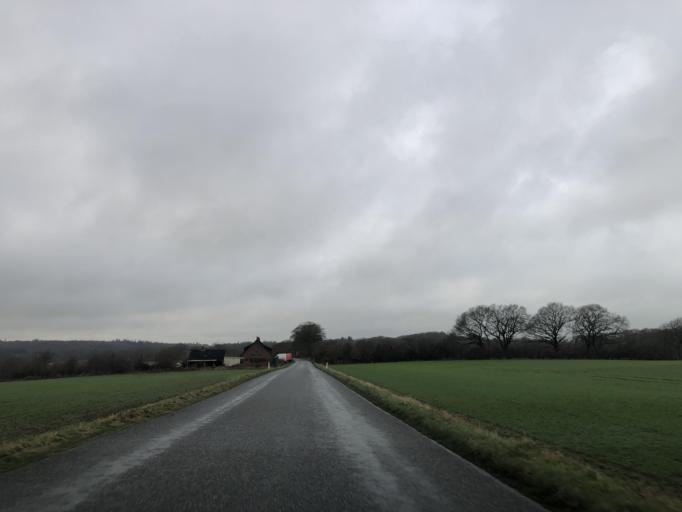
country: DK
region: Central Jutland
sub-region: Randers Kommune
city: Langa
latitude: 56.4787
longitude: 9.8632
